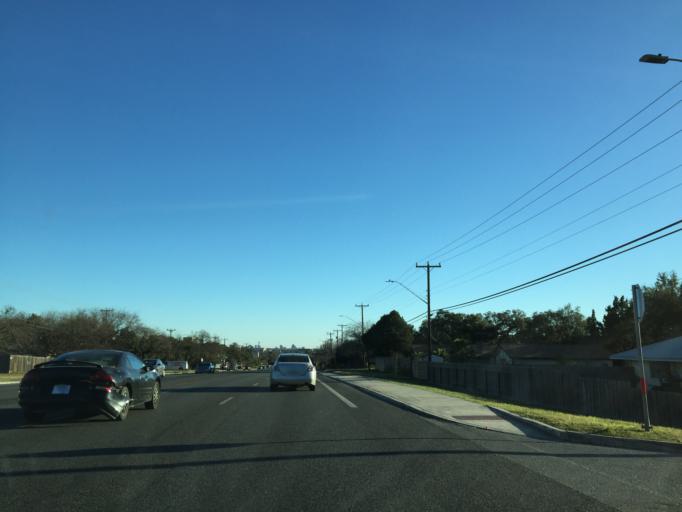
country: US
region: Texas
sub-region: Bexar County
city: Castle Hills
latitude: 29.5327
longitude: -98.5061
